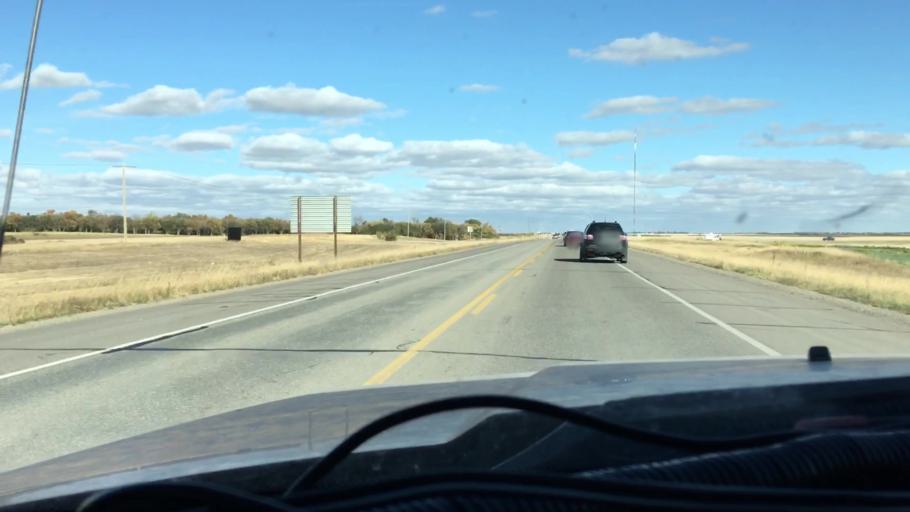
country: CA
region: Saskatchewan
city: Regina
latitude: 50.4837
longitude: -104.5326
